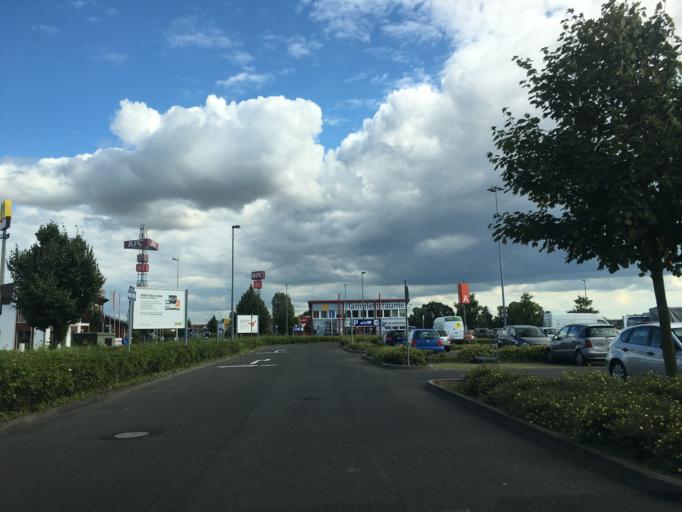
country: DE
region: North Rhine-Westphalia
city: Kamen
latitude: 51.5699
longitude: 7.6716
